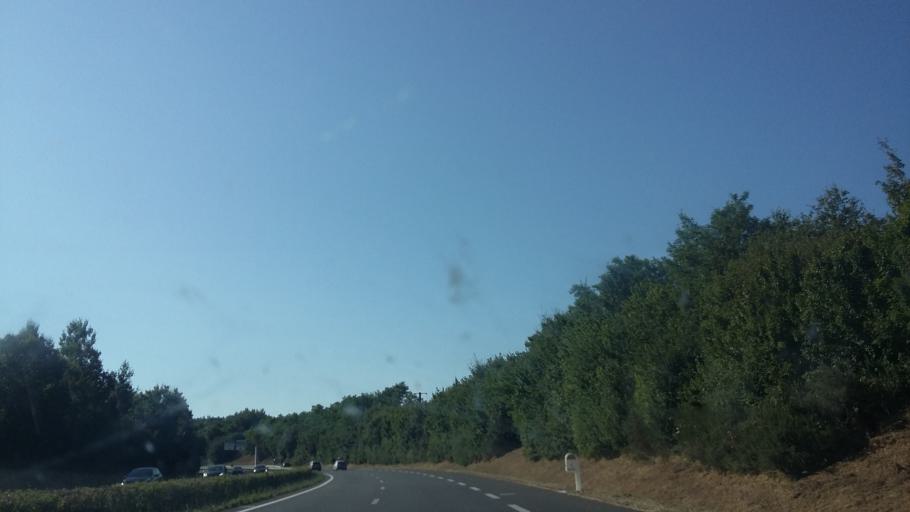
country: FR
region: Pays de la Loire
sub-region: Departement de la Vendee
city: Challans
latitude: 46.8611
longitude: -1.8578
